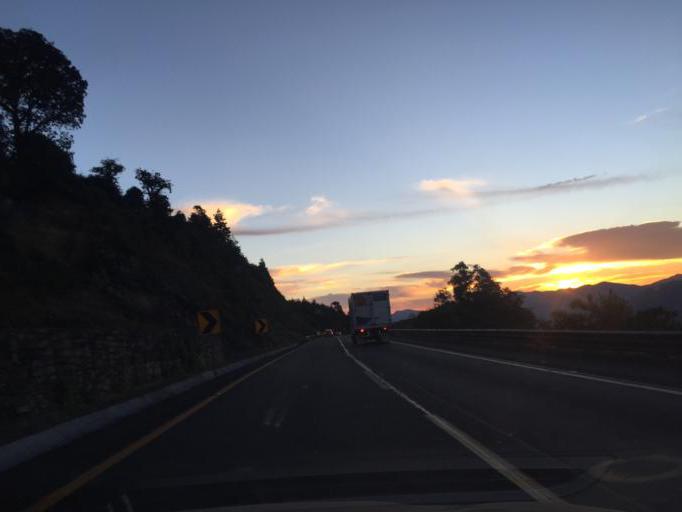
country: MX
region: Puebla
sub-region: Esperanza
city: San Jose Cuyachapa
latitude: 18.8254
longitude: -97.3130
